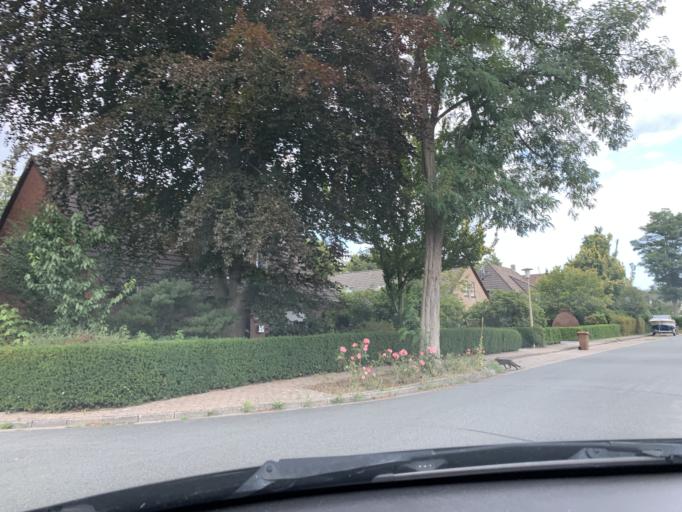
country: DE
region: Lower Saxony
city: Westerstede
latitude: 53.2568
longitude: 7.9386
